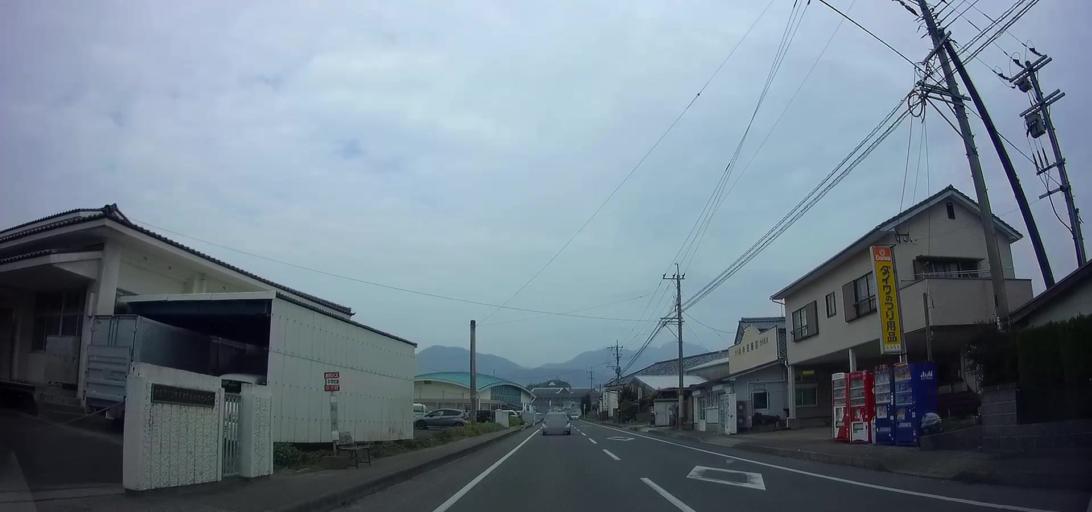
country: JP
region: Nagasaki
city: Shimabara
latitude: 32.6559
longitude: 130.2987
